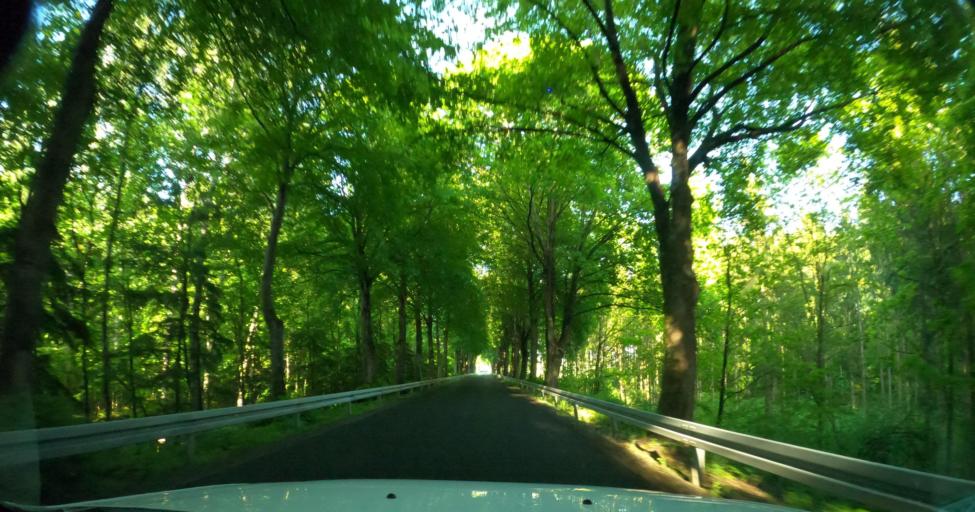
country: PL
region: Warmian-Masurian Voivodeship
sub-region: Powiat braniewski
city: Braniewo
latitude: 54.2826
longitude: 19.8575
